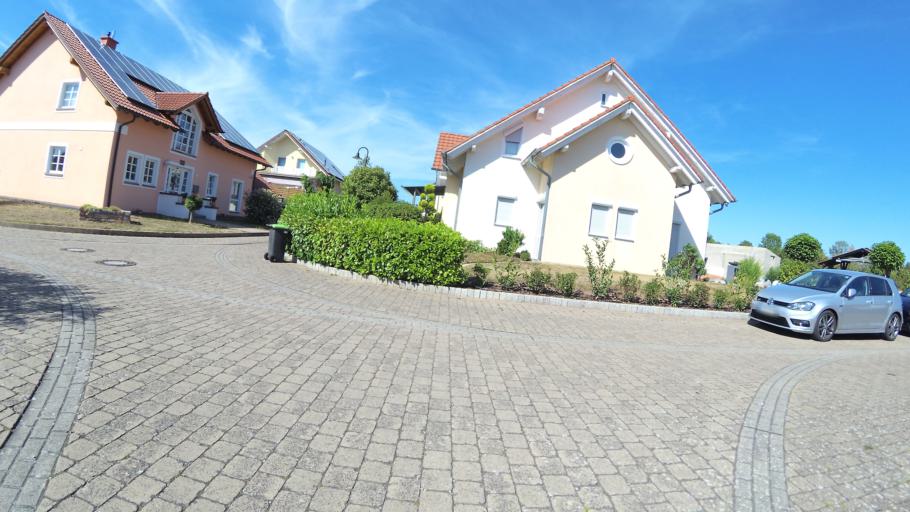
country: DE
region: Saarland
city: Gersheim
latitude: 49.1490
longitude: 7.2167
